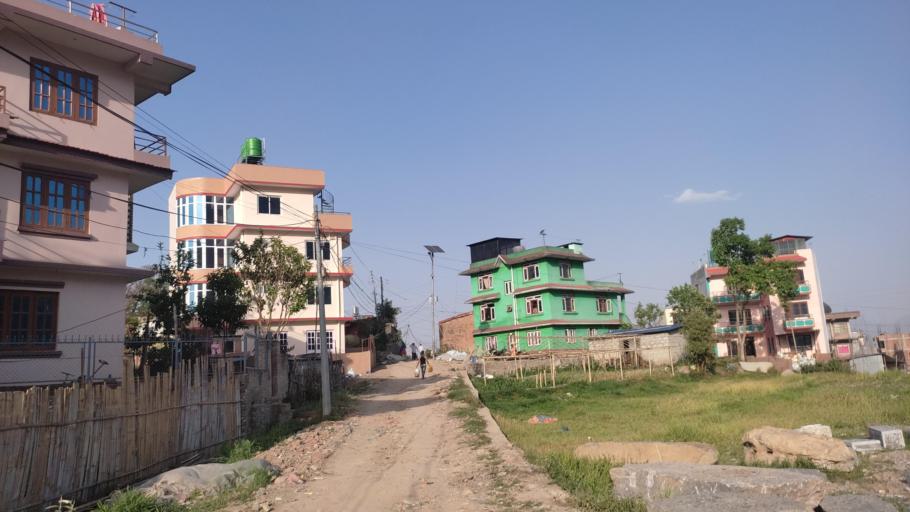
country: NP
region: Central Region
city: Kirtipur
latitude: 27.6639
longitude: 85.2654
